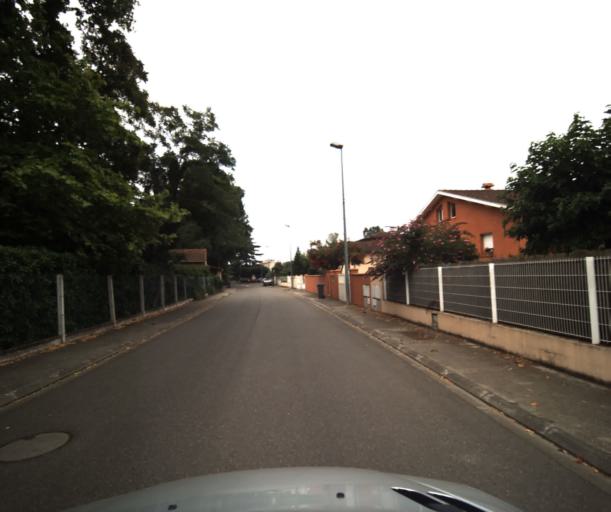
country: FR
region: Midi-Pyrenees
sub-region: Departement de la Haute-Garonne
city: Portet-sur-Garonne
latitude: 43.5288
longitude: 1.4144
